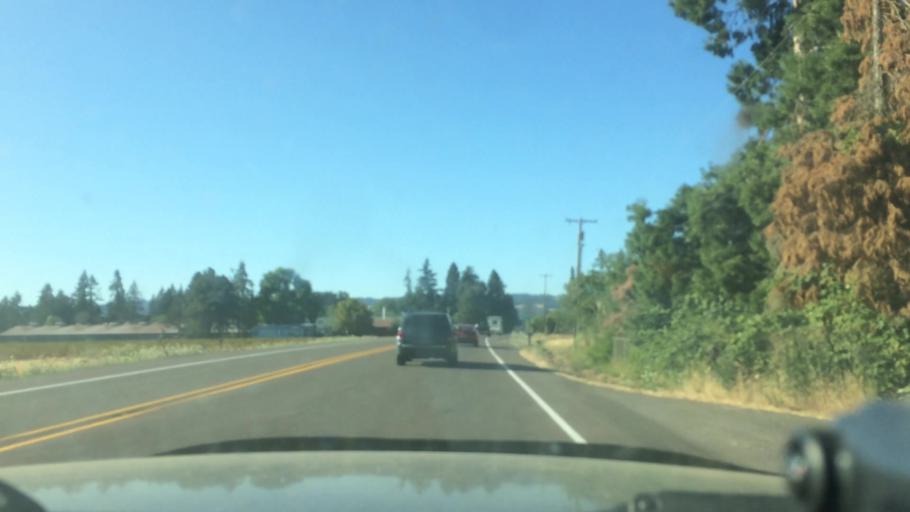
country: US
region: Oregon
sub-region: Yamhill County
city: Newberg
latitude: 45.2788
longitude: -122.9446
